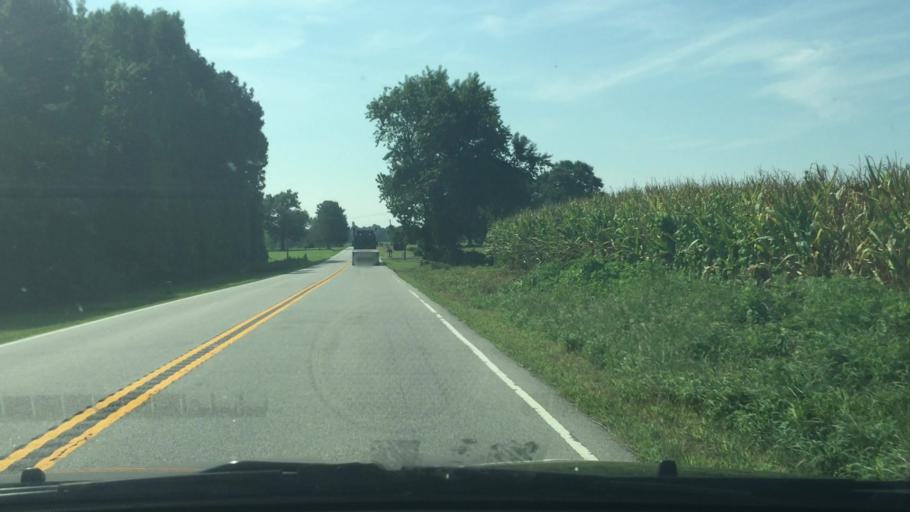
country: US
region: Virginia
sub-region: Sussex County
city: Sussex
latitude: 36.8809
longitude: -77.1520
